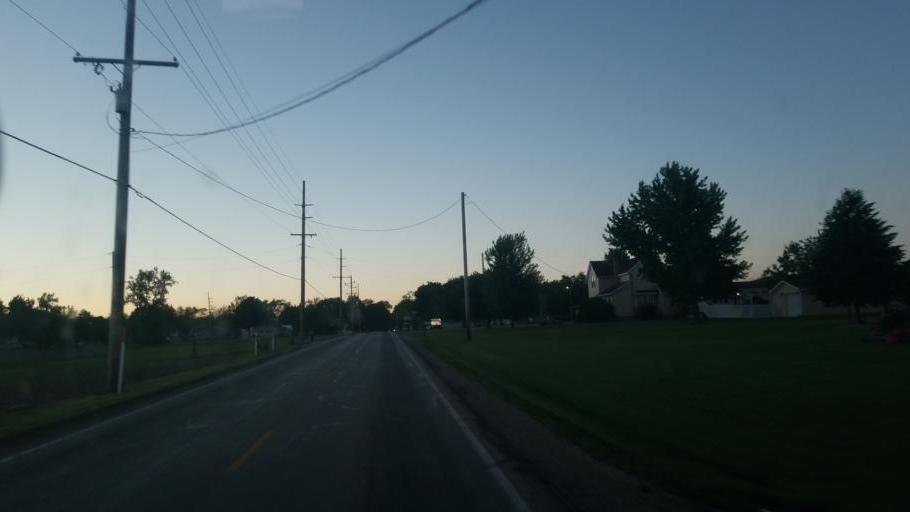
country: US
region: Indiana
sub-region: Elkhart County
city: Nappanee
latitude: 41.4332
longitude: -86.0014
